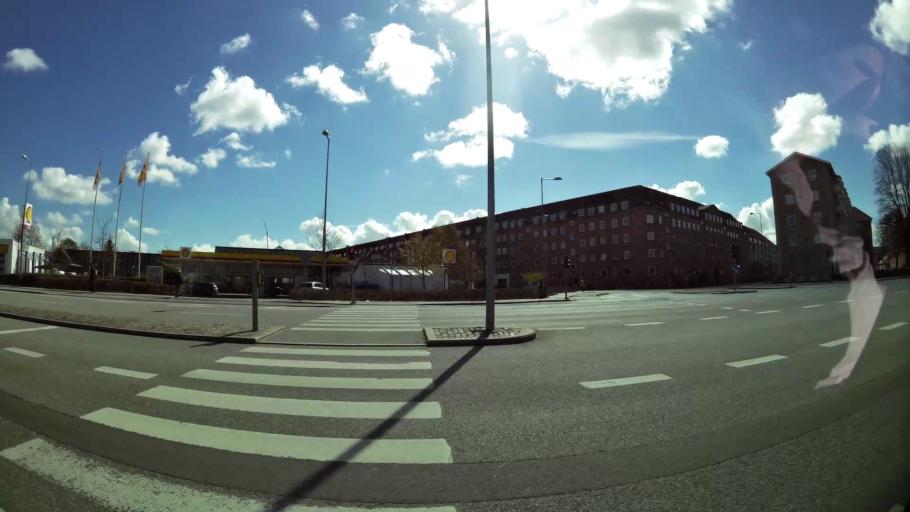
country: DK
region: North Denmark
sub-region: Alborg Kommune
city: Aalborg
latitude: 57.0429
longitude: 9.9336
